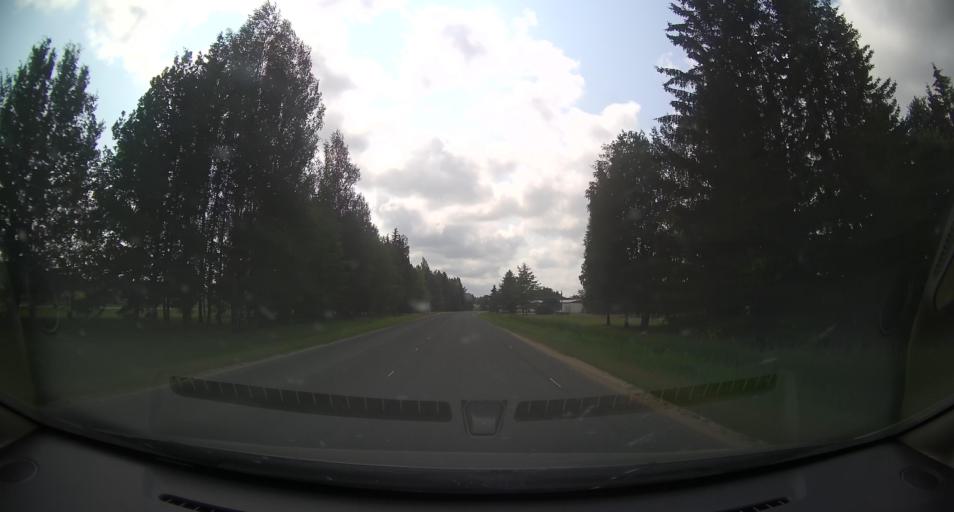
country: EE
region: Paernumaa
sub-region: Audru vald
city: Audru
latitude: 58.4755
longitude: 24.3277
